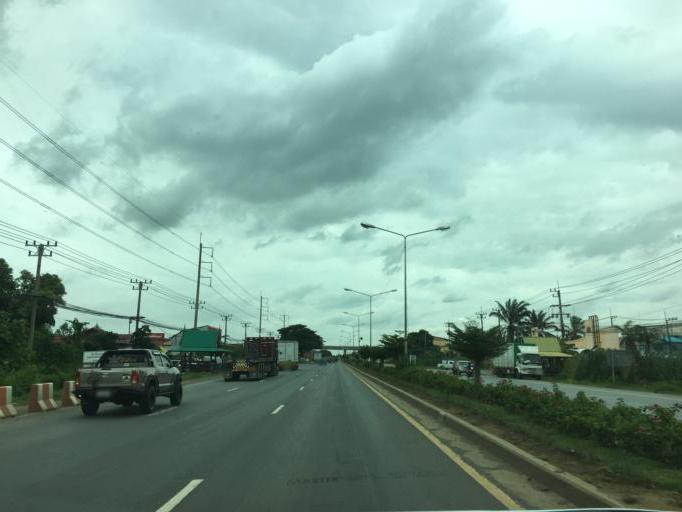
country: TH
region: Phra Nakhon Si Ayutthaya
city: Wang Noi
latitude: 14.2664
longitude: 100.6891
